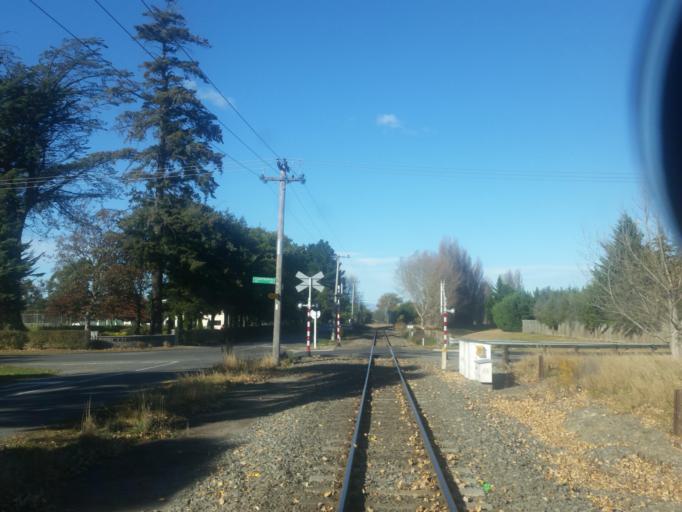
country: NZ
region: Canterbury
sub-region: Waimakariri District
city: Woodend
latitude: -43.2910
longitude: 172.5975
